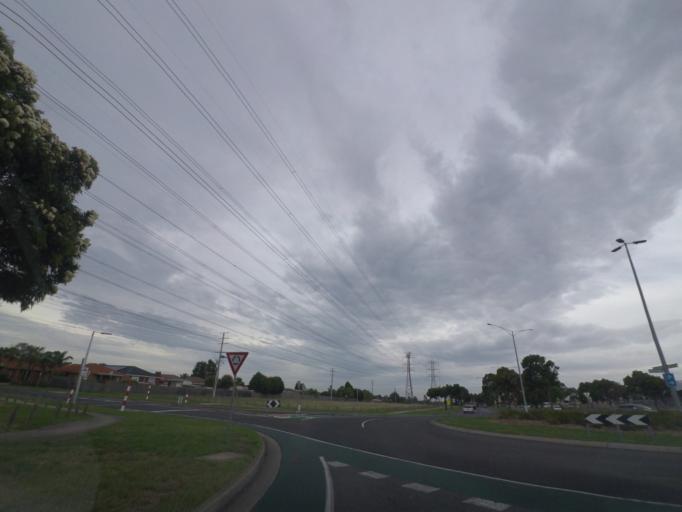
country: AU
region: Victoria
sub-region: Whittlesea
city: Mill Park
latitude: -37.6574
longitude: 145.0574
